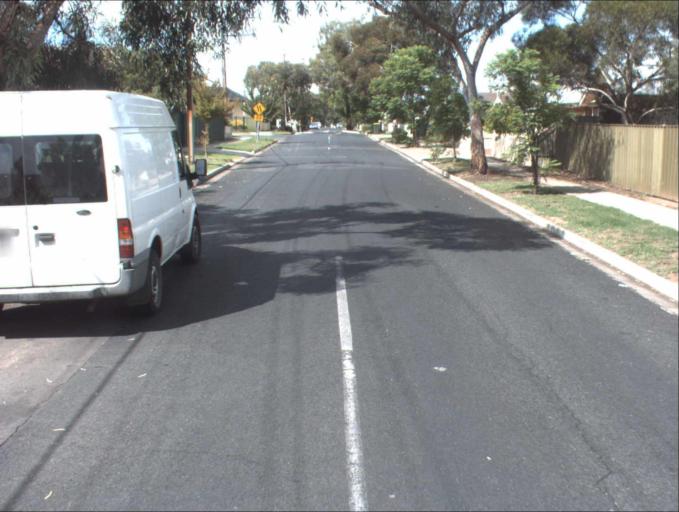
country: AU
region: South Australia
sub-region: Port Adelaide Enfield
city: Blair Athol
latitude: -34.8695
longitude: 138.6061
